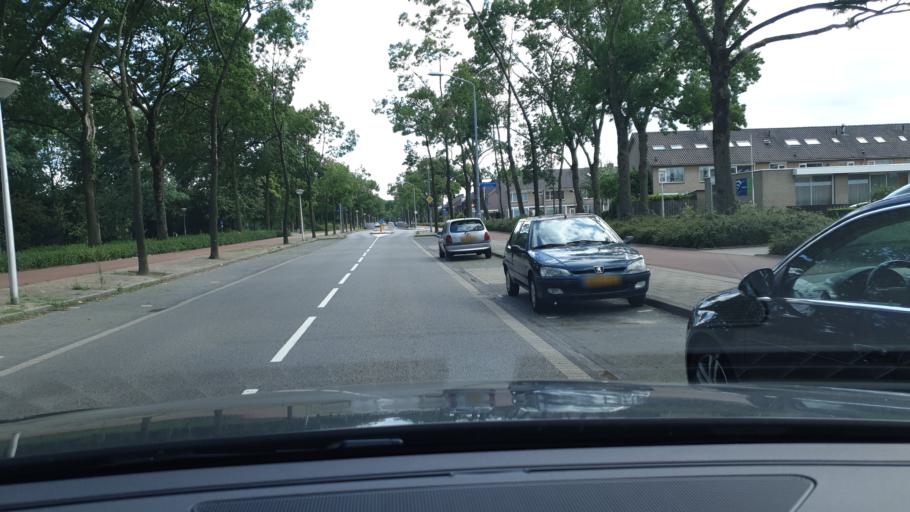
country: NL
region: North Brabant
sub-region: Gemeente Son en Breugel
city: Son
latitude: 51.4823
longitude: 5.4700
